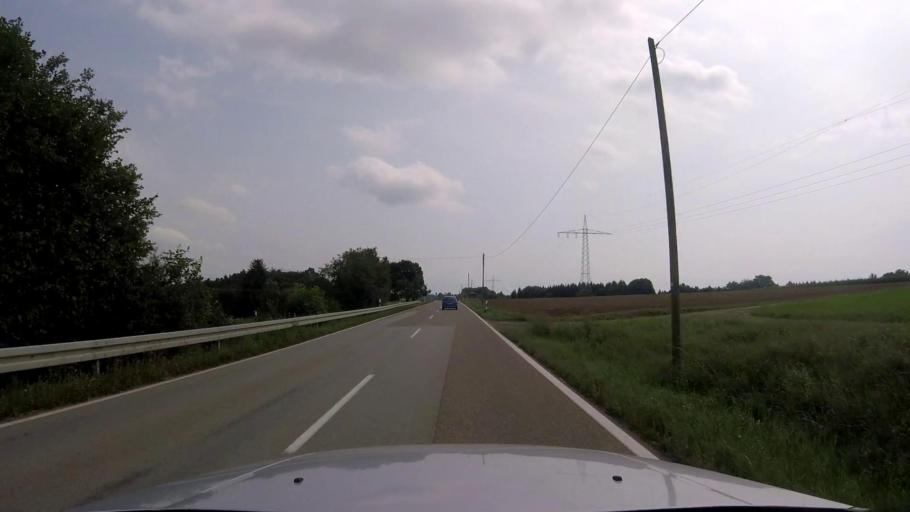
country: DE
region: Baden-Wuerttemberg
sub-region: Regierungsbezirk Stuttgart
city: Gschwend
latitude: 48.9068
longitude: 9.7476
